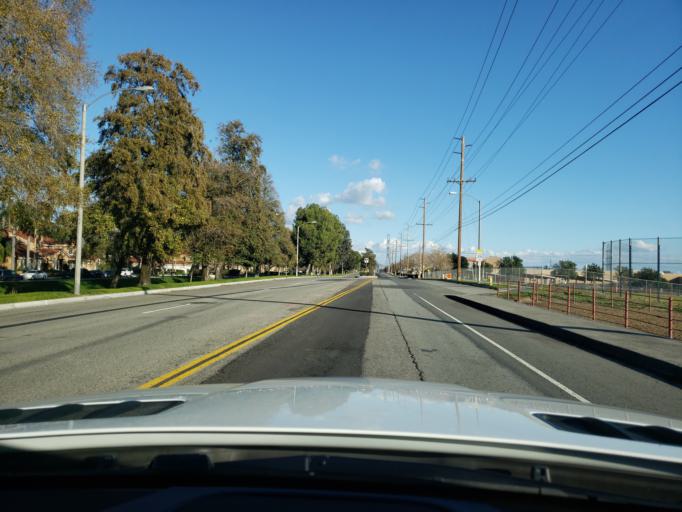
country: US
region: California
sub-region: Riverside County
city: Mira Loma
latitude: 34.0190
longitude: -117.5720
